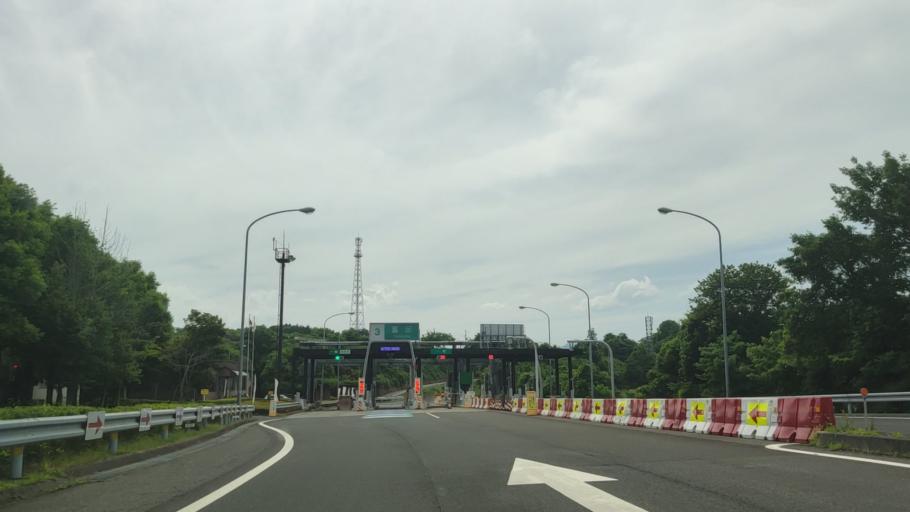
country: JP
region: Gunma
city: Tomioka
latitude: 36.2413
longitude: 138.8937
